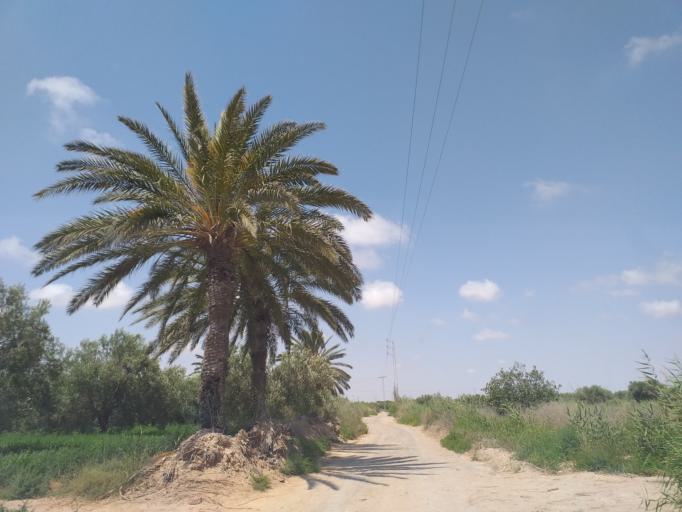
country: TN
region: Qabis
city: Gabes
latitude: 33.9525
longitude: 10.0442
